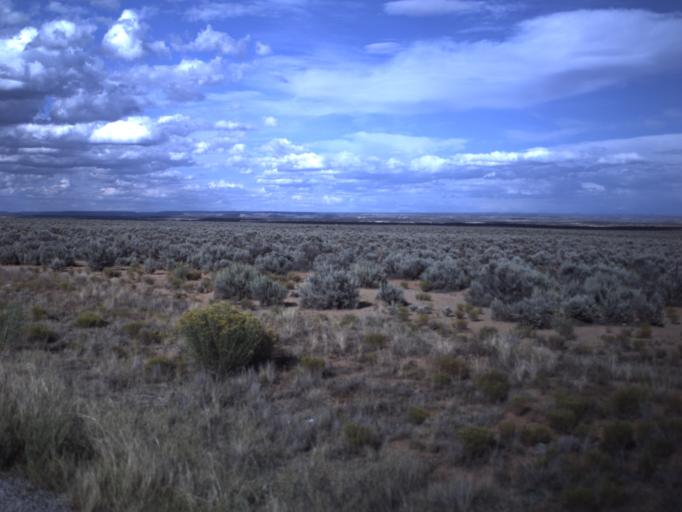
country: US
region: Utah
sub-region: San Juan County
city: Blanding
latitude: 37.3784
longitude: -109.3418
